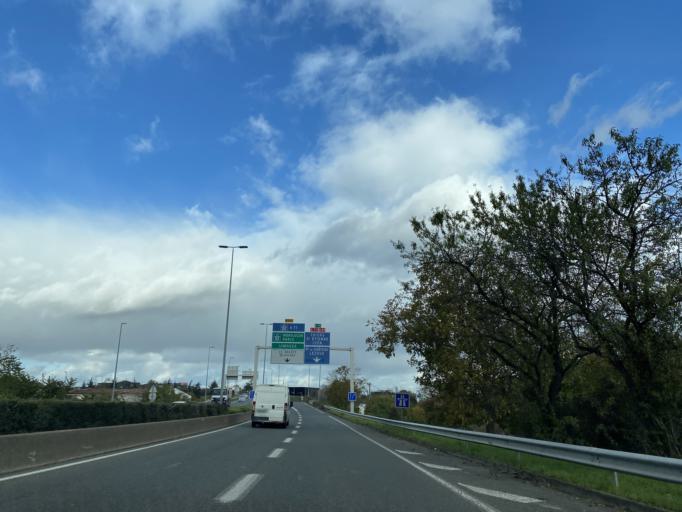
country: FR
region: Auvergne
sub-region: Departement du Puy-de-Dome
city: Aubiere
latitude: 45.7735
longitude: 3.1276
